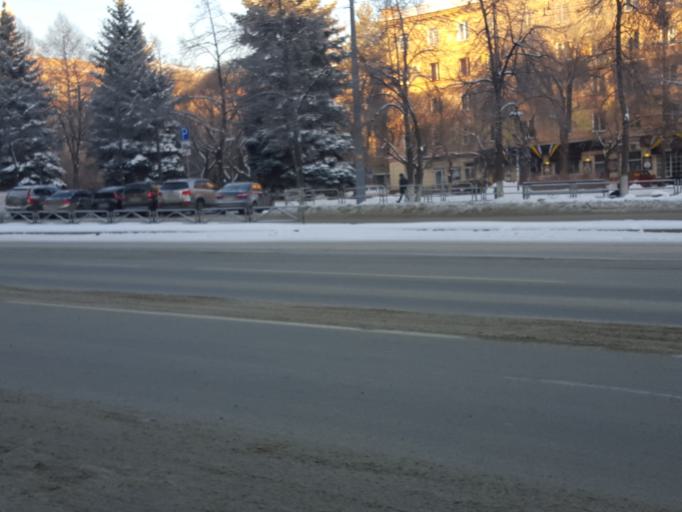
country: RU
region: Chelyabinsk
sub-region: Gorod Chelyabinsk
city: Chelyabinsk
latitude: 55.1594
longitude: 61.3742
